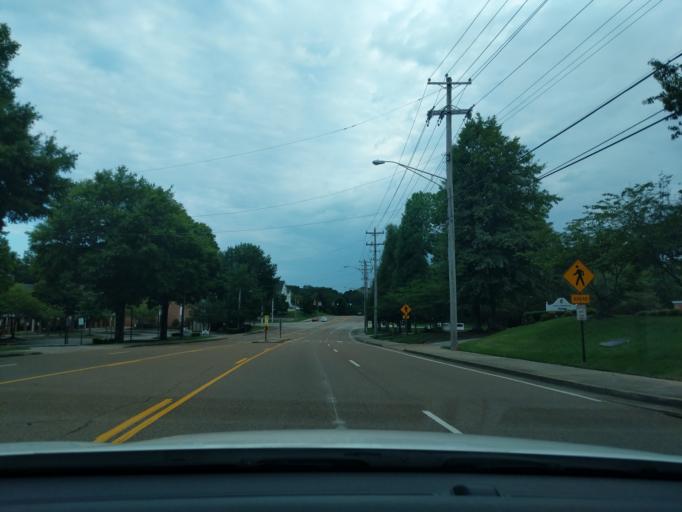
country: US
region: Tennessee
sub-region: Shelby County
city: Germantown
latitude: 35.0864
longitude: -89.8116
